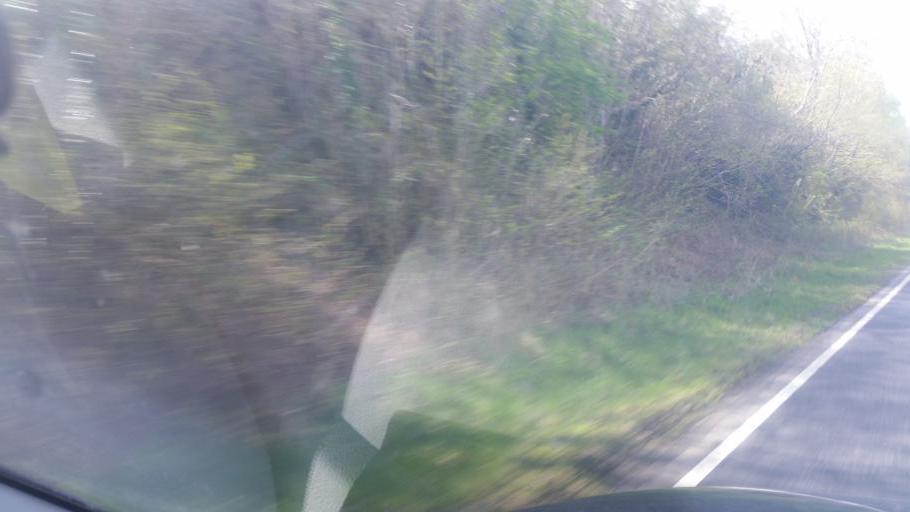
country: GB
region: Northern Ireland
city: Irvinestown
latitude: 54.4225
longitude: -7.7435
